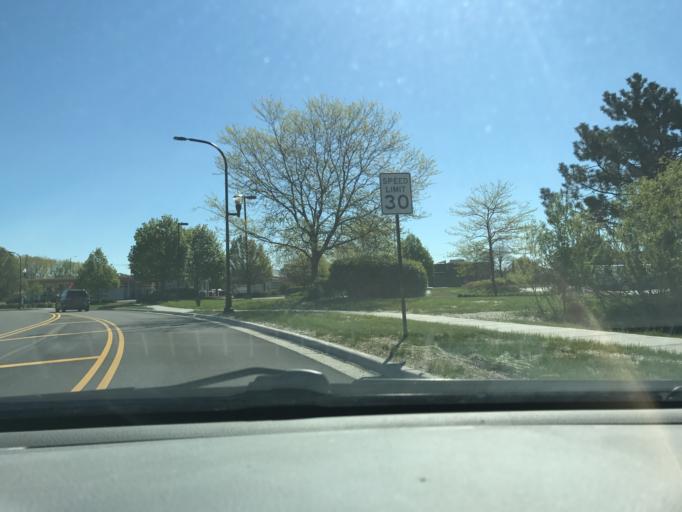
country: US
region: Illinois
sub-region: Kane County
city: South Elgin
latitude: 42.0244
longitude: -88.3414
